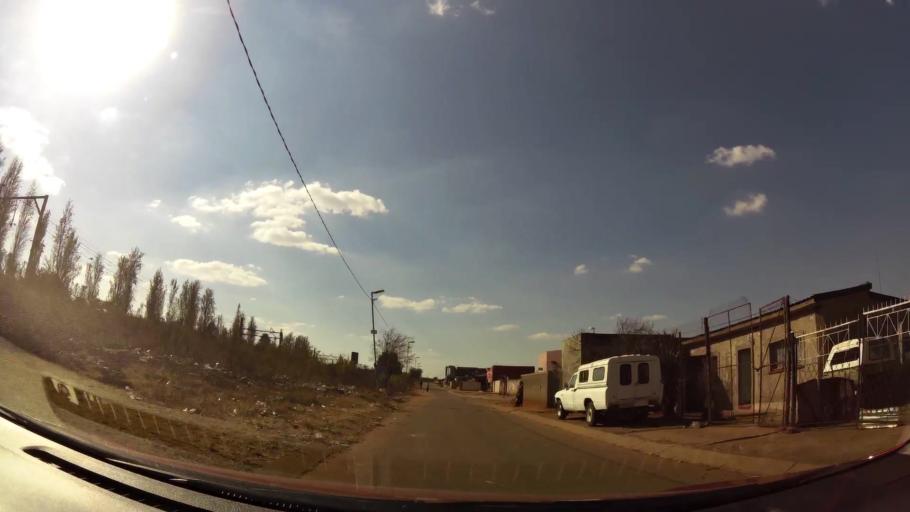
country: ZA
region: Gauteng
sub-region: City of Johannesburg Metropolitan Municipality
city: Soweto
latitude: -26.2354
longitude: 27.8738
